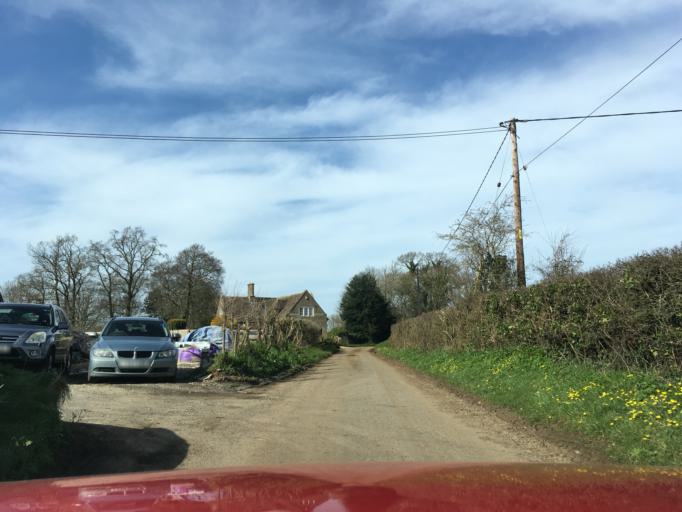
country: GB
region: England
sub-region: Wiltshire
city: Chippenham
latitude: 51.4902
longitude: -2.1424
